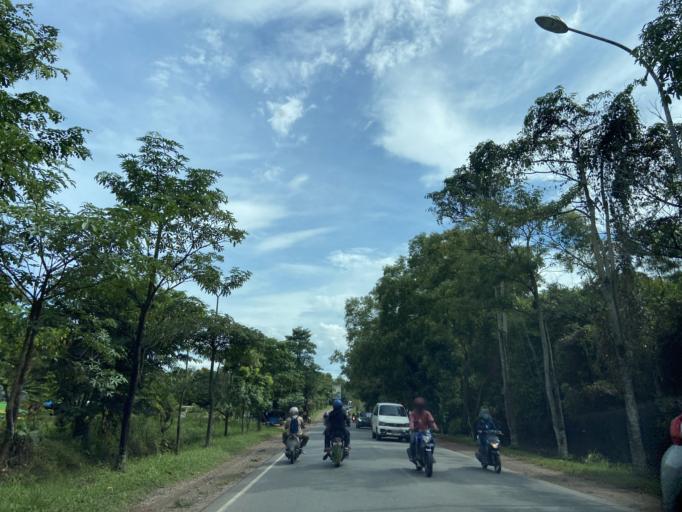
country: SG
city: Singapore
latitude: 1.0551
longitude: 103.9588
